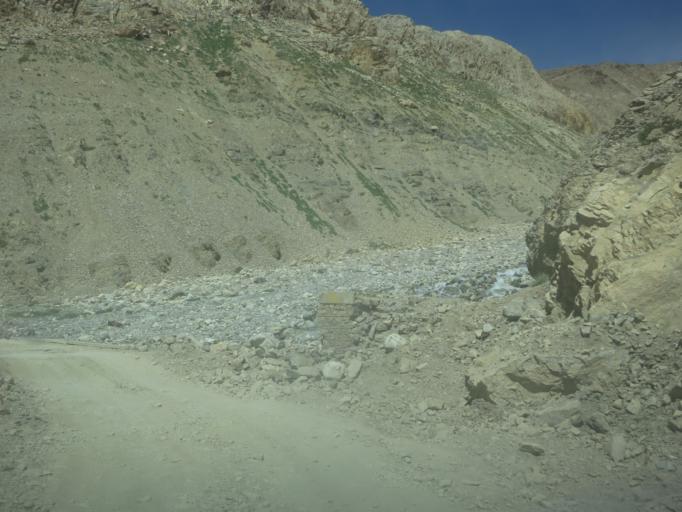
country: IN
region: Himachal Pradesh
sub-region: Kulu
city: Manali
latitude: 32.4298
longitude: 77.6753
